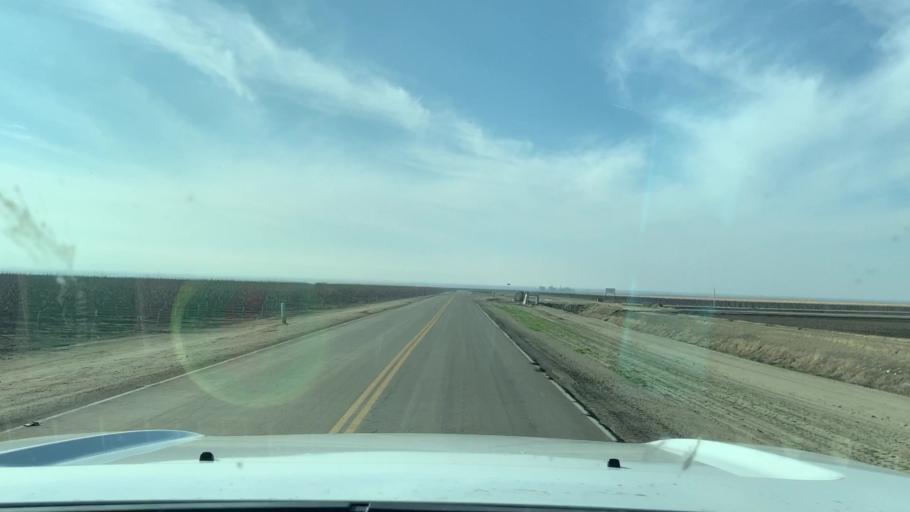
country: US
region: California
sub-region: Kern County
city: Buttonwillow
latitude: 35.4536
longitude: -119.5631
